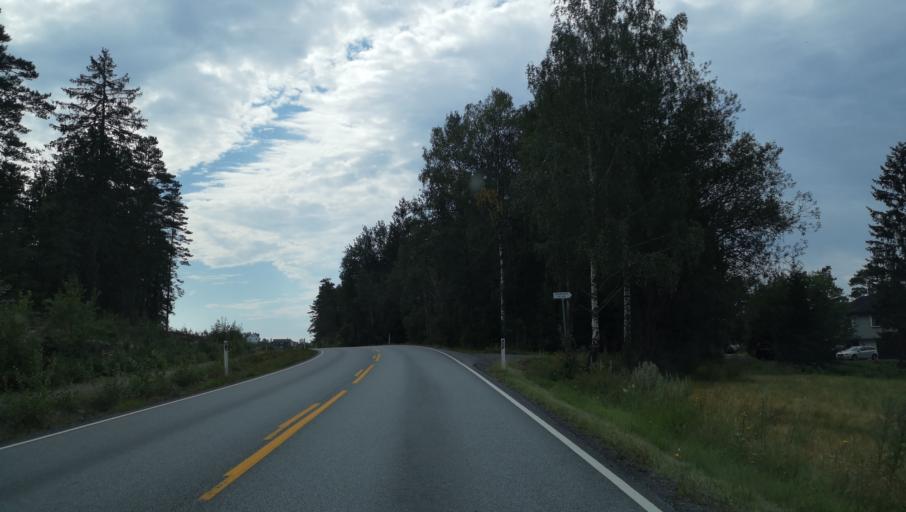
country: NO
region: Ostfold
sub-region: Valer
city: Kirkebygda
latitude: 59.4721
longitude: 10.7857
